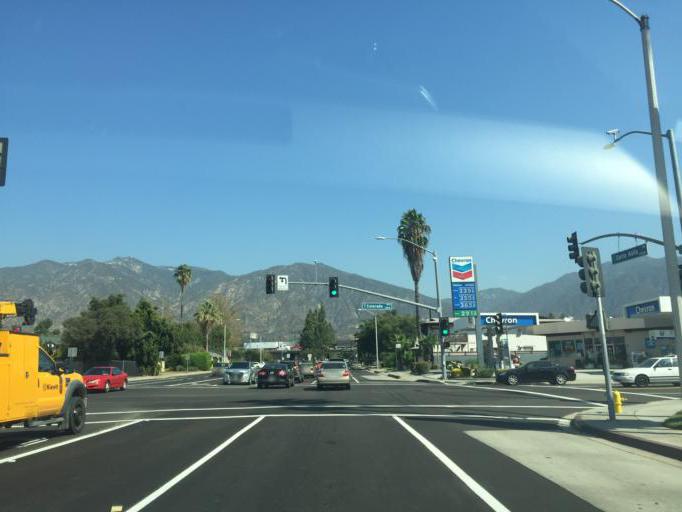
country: US
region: California
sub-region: Los Angeles County
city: Arcadia
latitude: 34.1452
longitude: -118.0315
